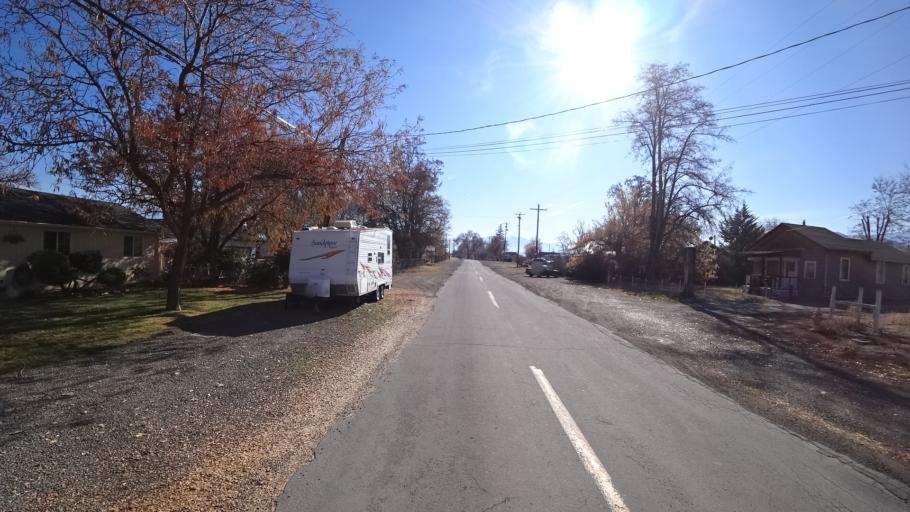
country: US
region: California
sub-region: Siskiyou County
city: Montague
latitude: 41.6418
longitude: -122.5224
